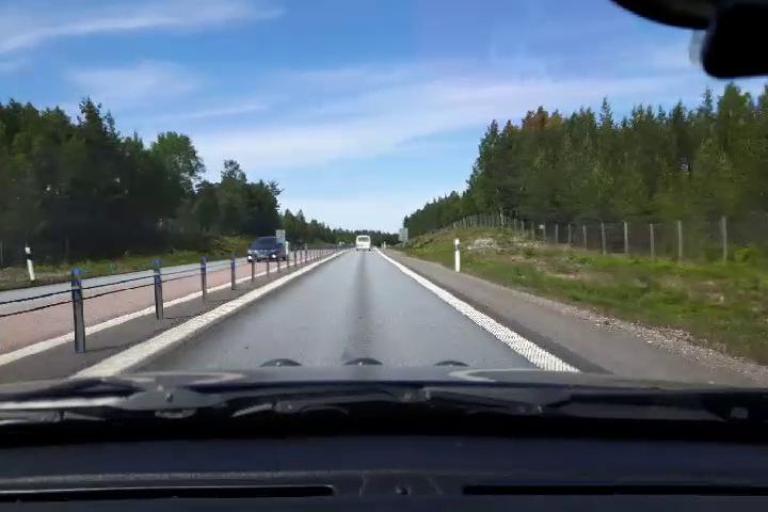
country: SE
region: Gaevleborg
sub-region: Gavle Kommun
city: Gavle
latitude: 60.8058
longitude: 17.0819
